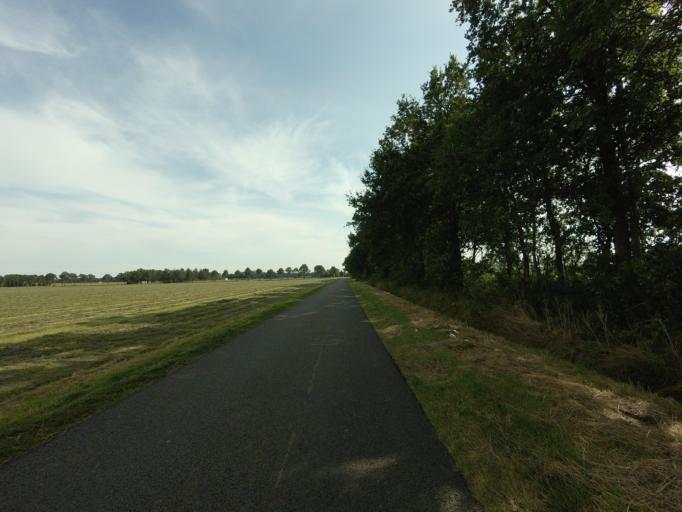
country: NL
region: Drenthe
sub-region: Gemeente Coevorden
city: Dalen
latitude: 52.6979
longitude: 6.7323
